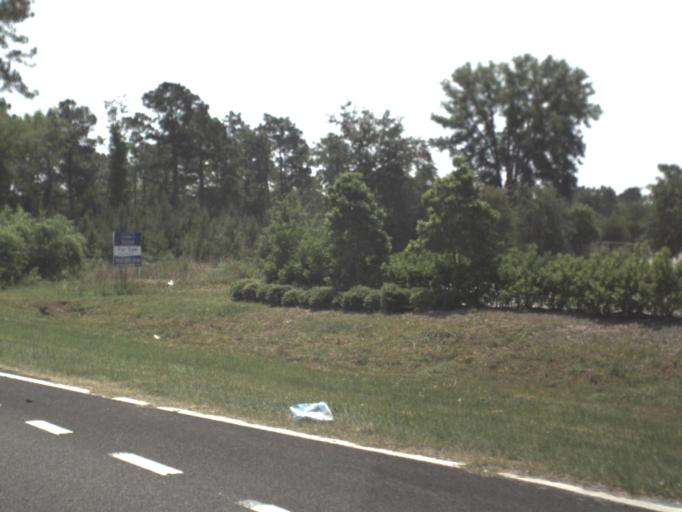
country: US
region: Florida
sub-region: Nassau County
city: Yulee
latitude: 30.6305
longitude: -81.5837
